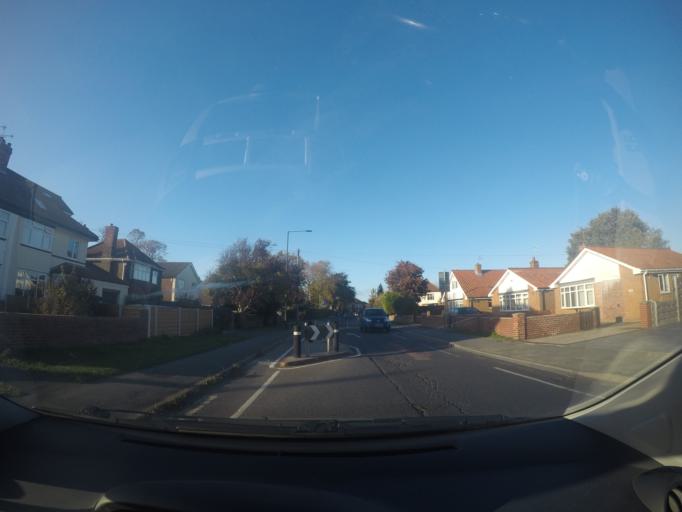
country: GB
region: England
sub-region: City of York
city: Huntington
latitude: 53.9843
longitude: -1.0691
